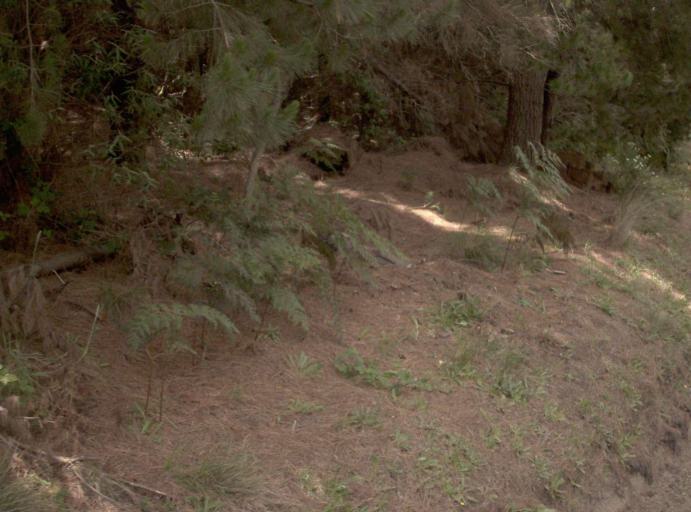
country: AU
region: Victoria
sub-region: Latrobe
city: Traralgon
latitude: -38.4150
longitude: 146.6175
